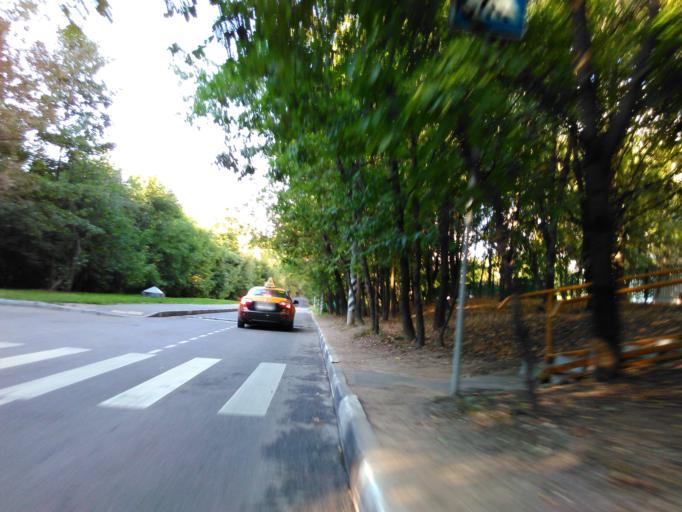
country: RU
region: Moscow
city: Troparevo
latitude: 55.6484
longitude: 37.5170
